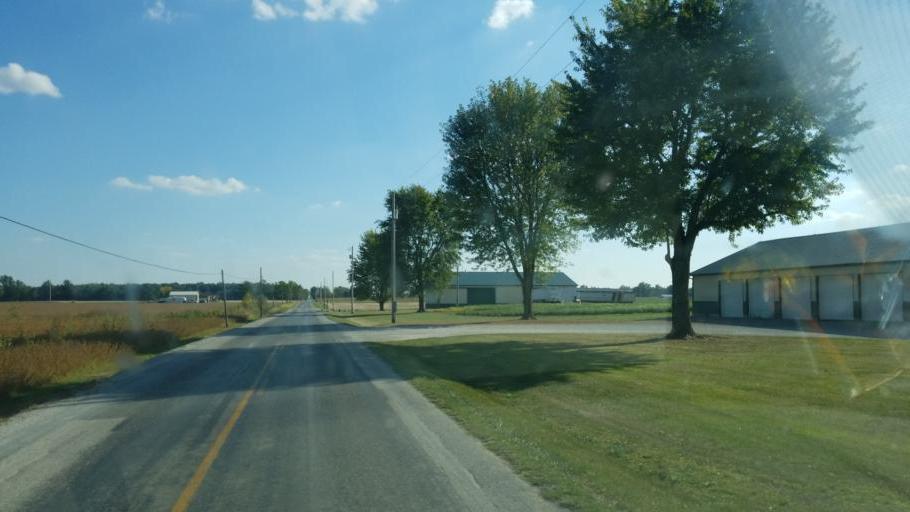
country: US
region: Ohio
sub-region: Union County
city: Richwood
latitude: 40.5508
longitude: -83.3902
